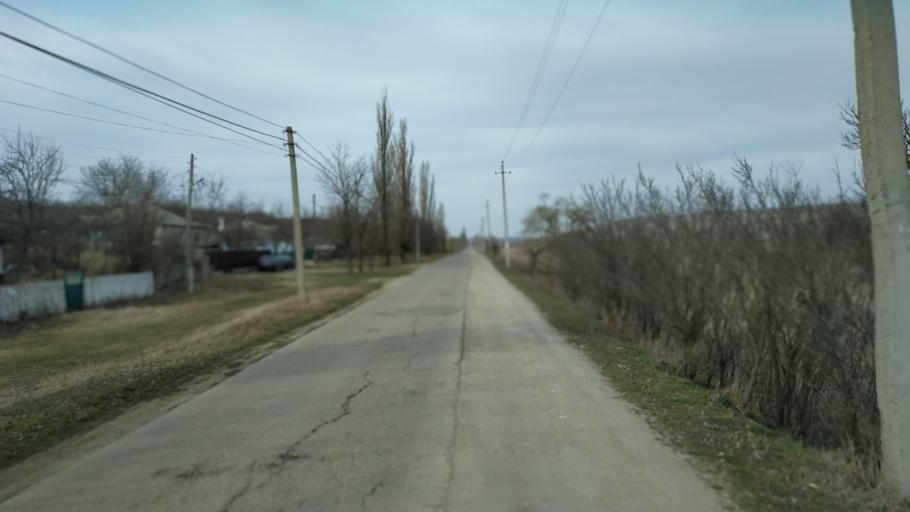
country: RO
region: Vaslui
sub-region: Comuna Dranceni
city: Dranceni
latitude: 46.8646
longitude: 28.2008
